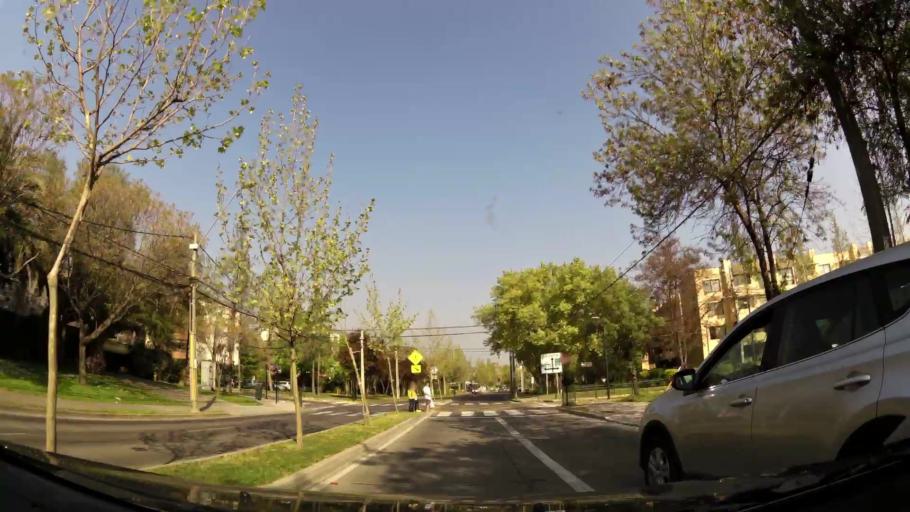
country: CL
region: Santiago Metropolitan
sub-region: Provincia de Santiago
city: Villa Presidente Frei, Nunoa, Santiago, Chile
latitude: -33.3826
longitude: -70.5519
